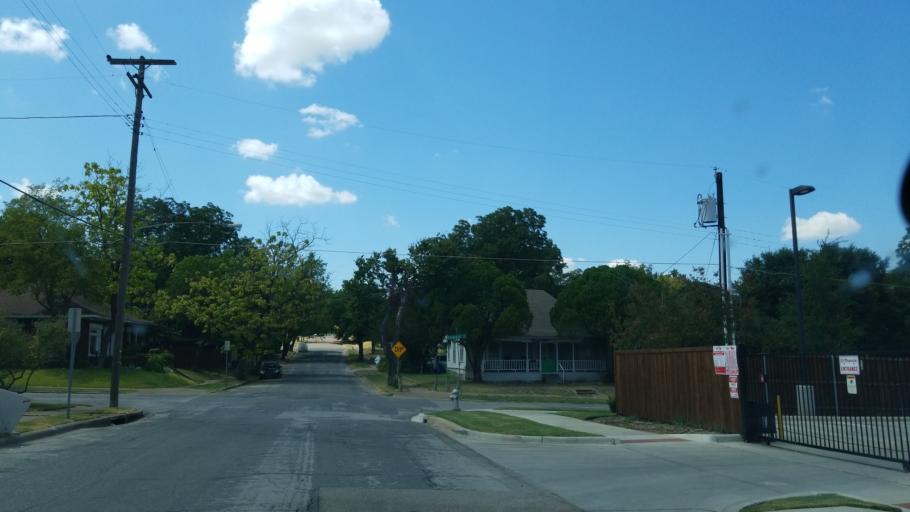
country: US
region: Texas
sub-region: Dallas County
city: Dallas
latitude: 32.7538
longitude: -96.8250
